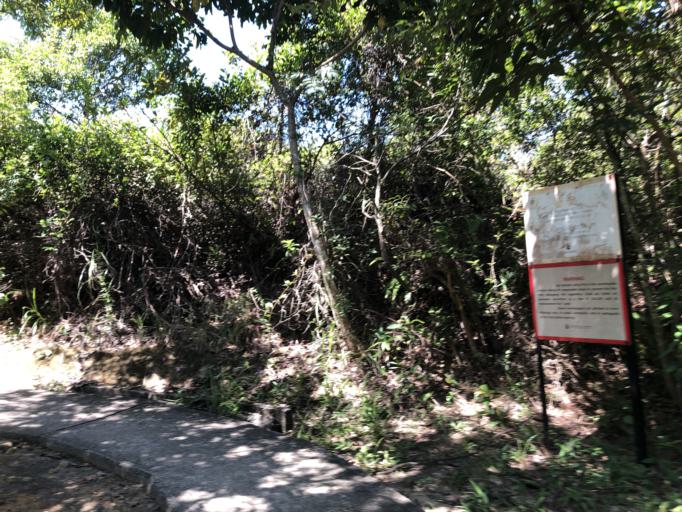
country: HK
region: Tuen Mun
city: Tuen Mun
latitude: 22.2833
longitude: 113.9835
